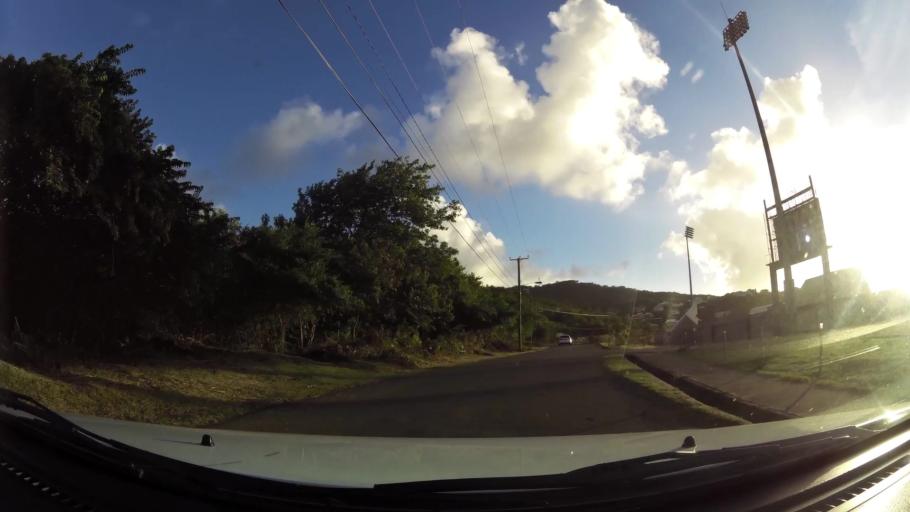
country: LC
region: Gros-Islet
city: Gros Islet
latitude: 14.0708
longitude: -60.9304
